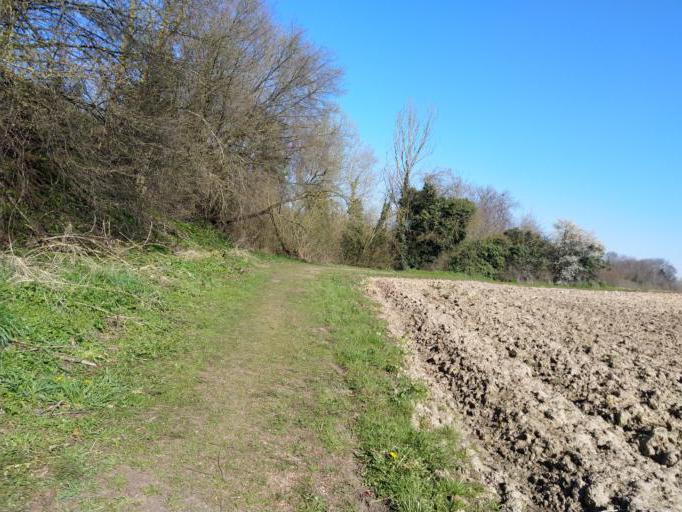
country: BE
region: Wallonia
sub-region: Province du Hainaut
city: Lens
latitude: 50.5544
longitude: 3.9060
